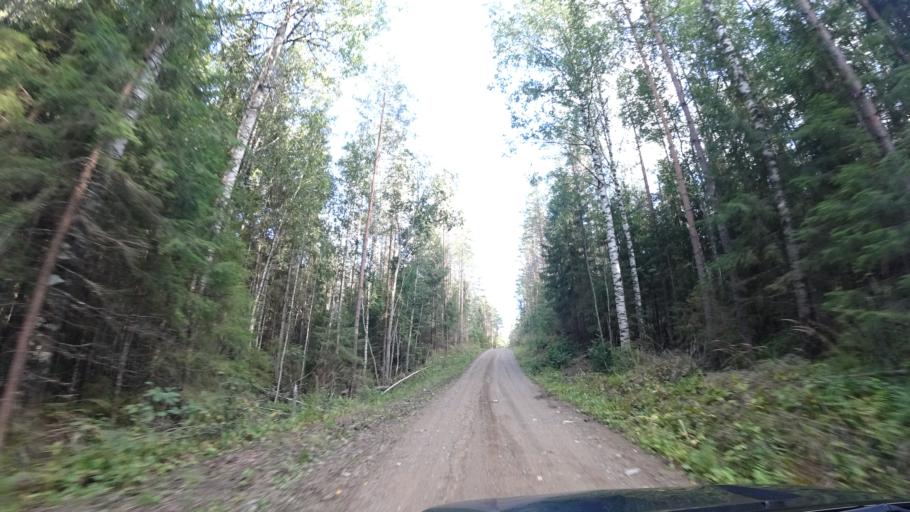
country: FI
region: Paijanne Tavastia
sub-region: Lahti
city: Auttoinen
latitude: 61.2238
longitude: 25.1969
